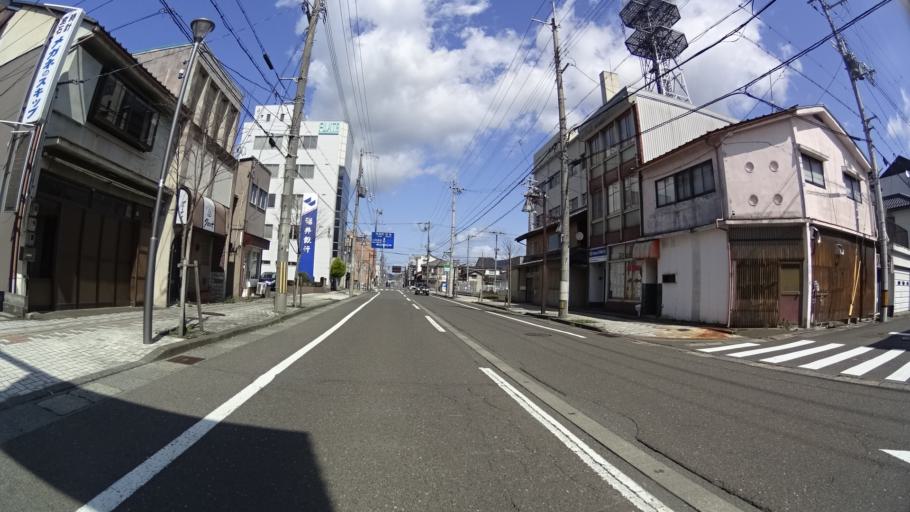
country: JP
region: Fukui
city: Obama
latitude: 35.4984
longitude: 135.7459
